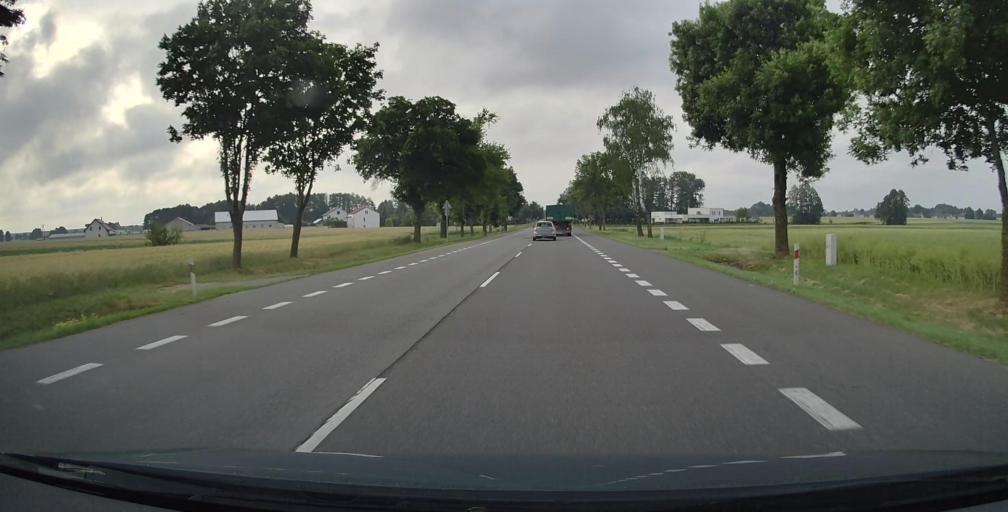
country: PL
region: Masovian Voivodeship
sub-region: Powiat siedlecki
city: Zbuczyn
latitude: 52.0945
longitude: 22.4194
